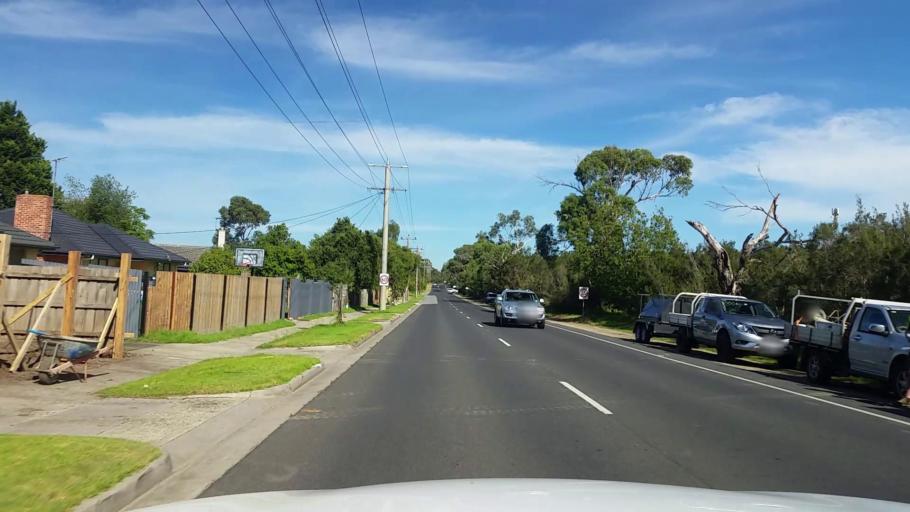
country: AU
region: Victoria
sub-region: Mornington Peninsula
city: Baxter
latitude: -38.1953
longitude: 145.1449
